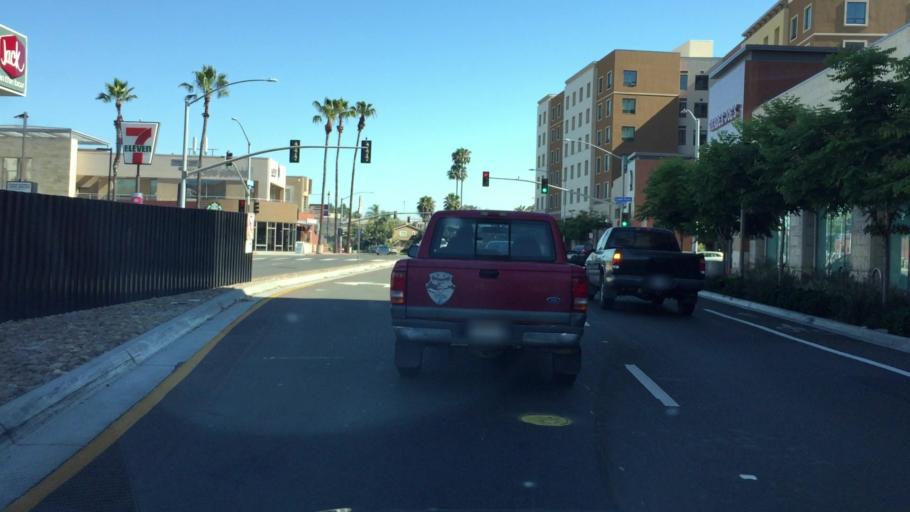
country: US
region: California
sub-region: San Diego County
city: La Mesa
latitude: 32.7722
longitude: -117.0700
